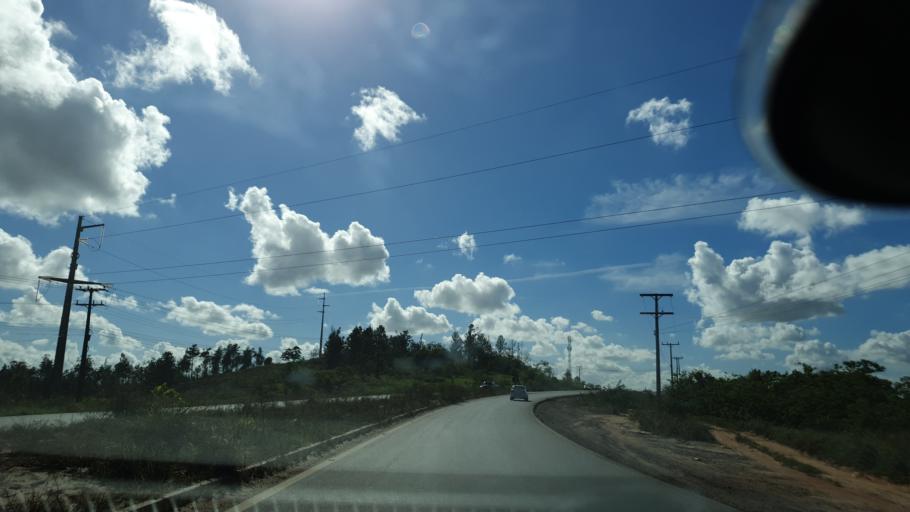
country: BR
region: Bahia
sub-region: Camacari
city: Camacari
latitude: -12.6851
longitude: -38.2716
